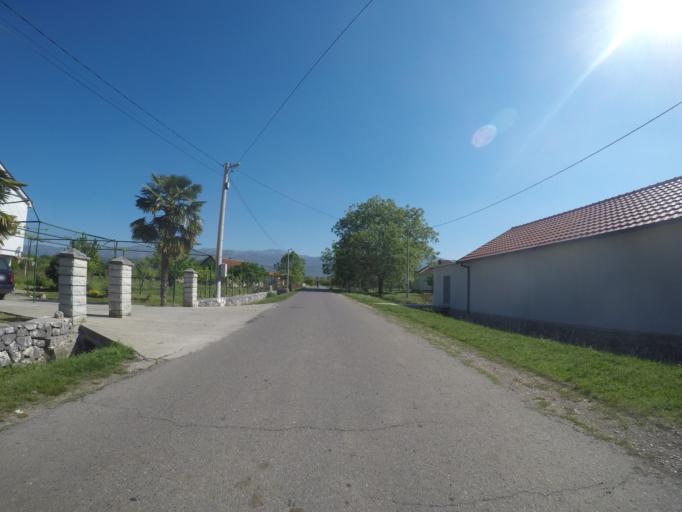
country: ME
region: Danilovgrad
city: Danilovgrad
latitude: 42.5391
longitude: 19.0923
